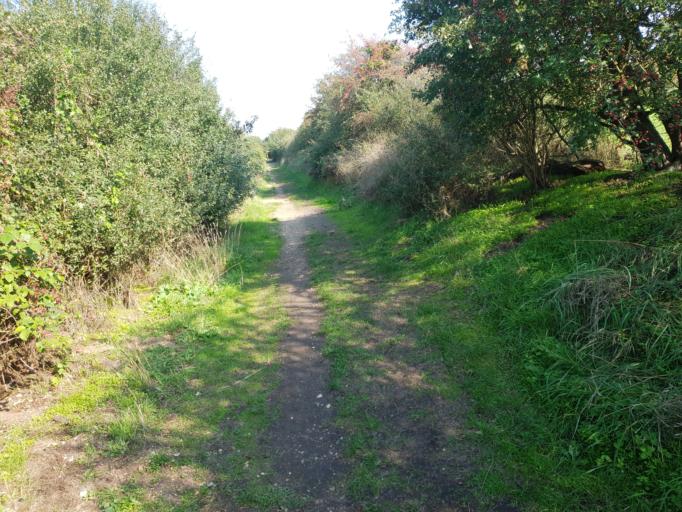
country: GB
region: England
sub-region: Essex
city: Manningtree
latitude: 51.9525
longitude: 1.0350
